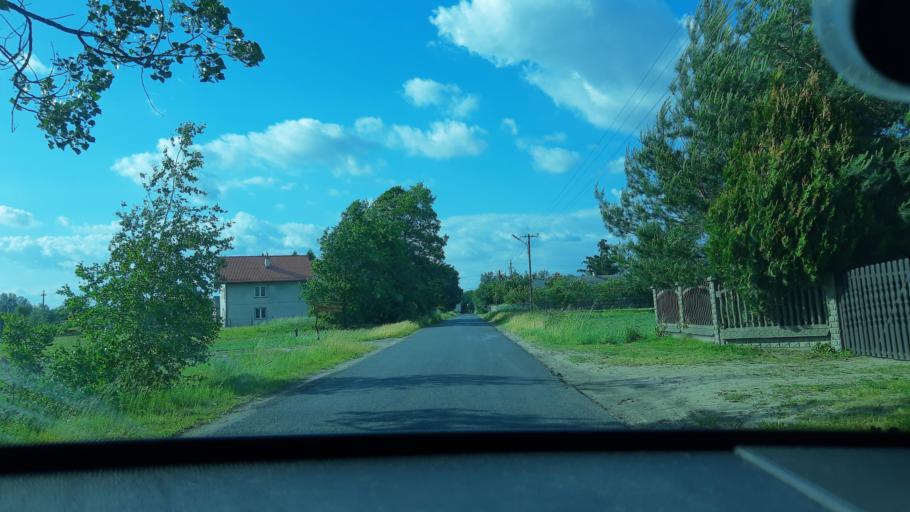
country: PL
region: Lodz Voivodeship
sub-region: Powiat zdunskowolski
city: Zapolice
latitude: 51.5216
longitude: 18.8436
